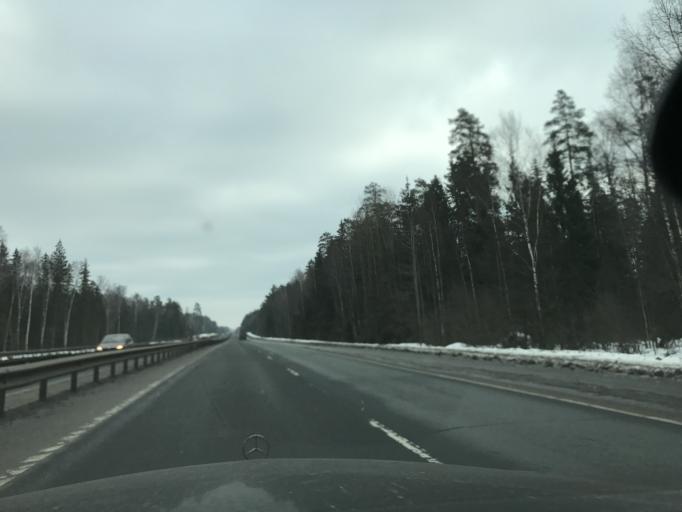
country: RU
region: Vladimir
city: Stepantsevo
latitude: 56.2273
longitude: 41.6639
